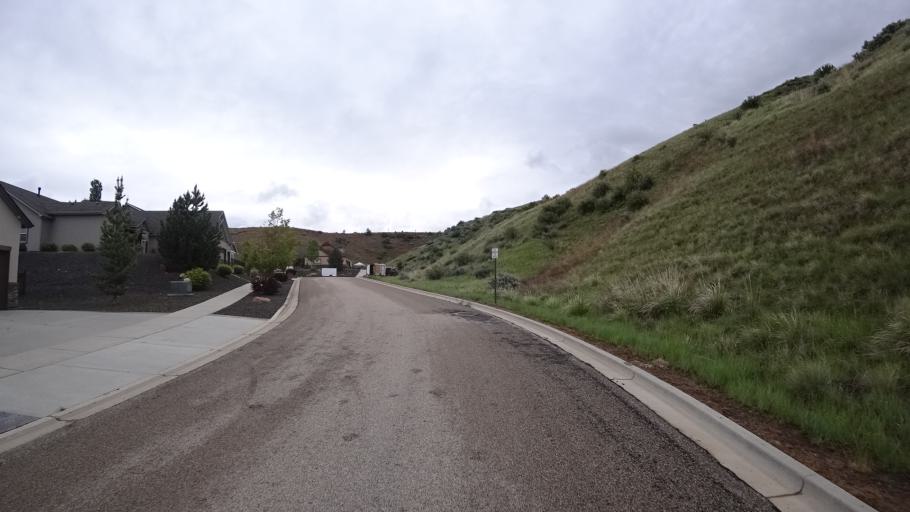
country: US
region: Idaho
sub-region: Ada County
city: Eagle
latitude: 43.7676
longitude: -116.2612
